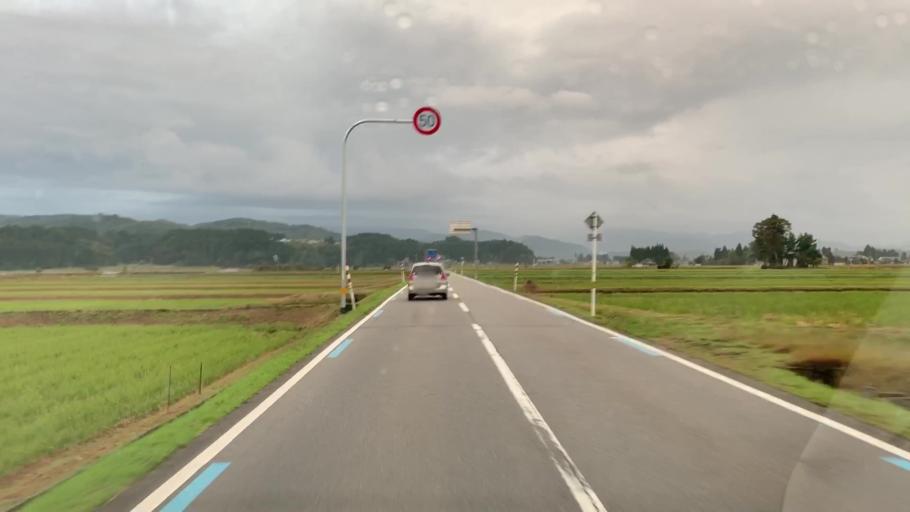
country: JP
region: Toyama
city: Kamiichi
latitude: 36.6293
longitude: 137.3286
